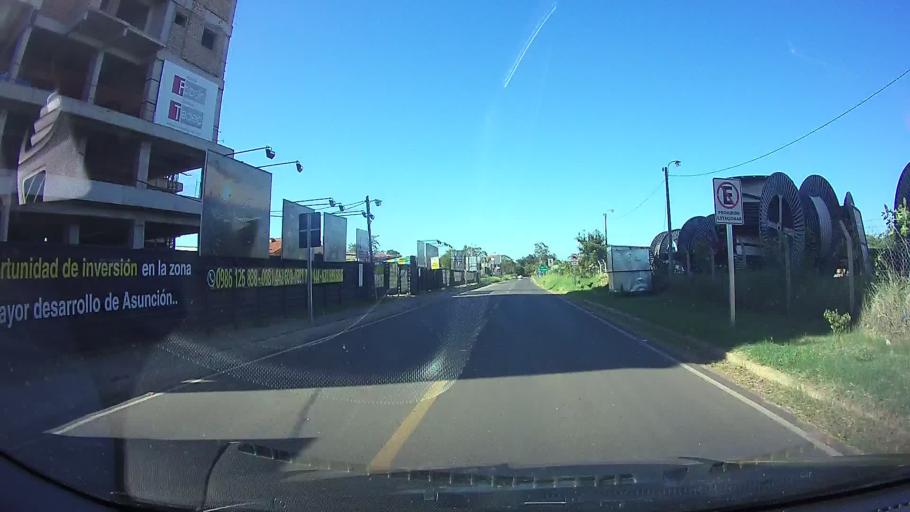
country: PY
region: Central
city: Fernando de la Mora
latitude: -25.2892
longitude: -57.5423
